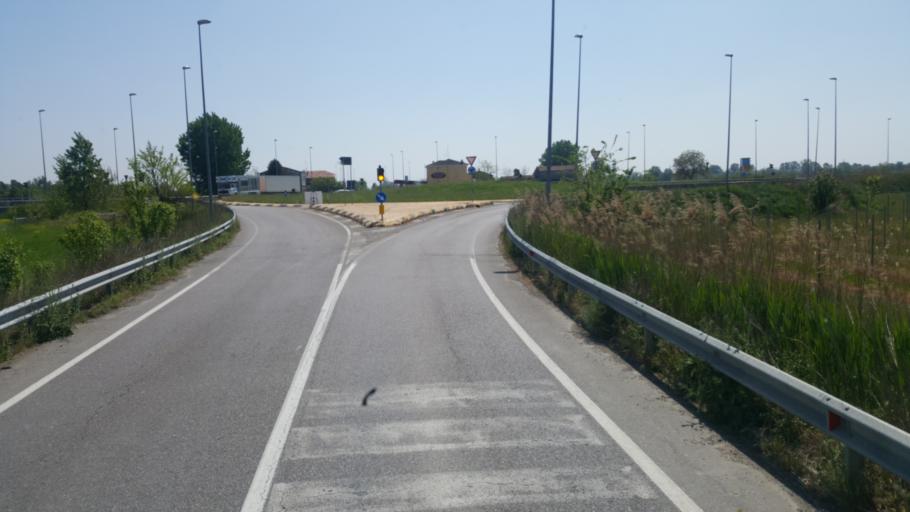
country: IT
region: Lombardy
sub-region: Provincia di Mantova
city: San Benedetto Po
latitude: 45.0075
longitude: 10.9328
